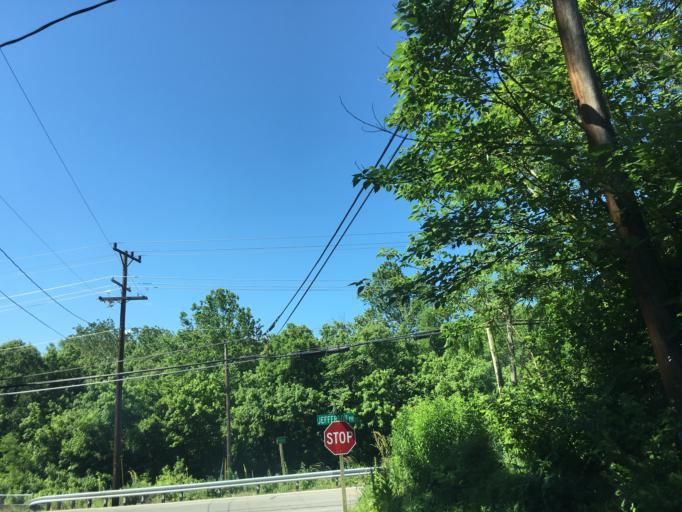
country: US
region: Maryland
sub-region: Frederick County
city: Brunswick
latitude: 39.3285
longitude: -77.6675
